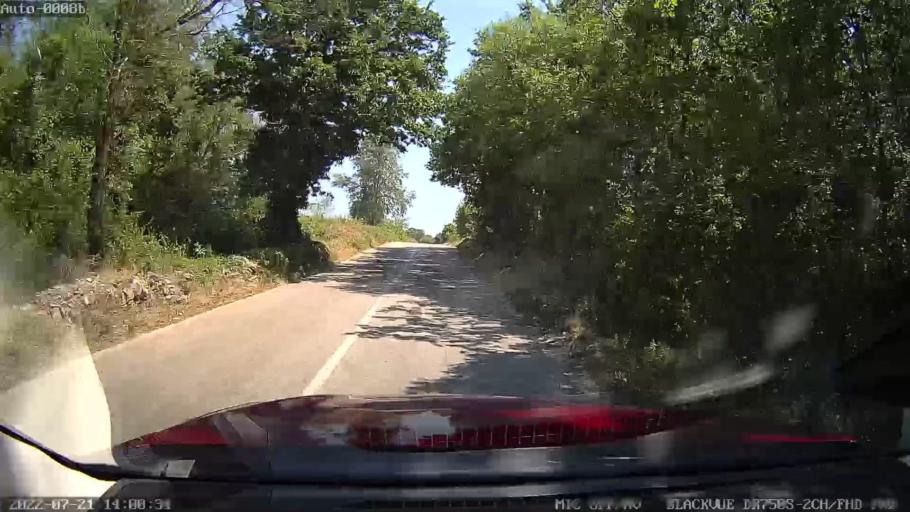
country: HR
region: Istarska
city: Vodnjan
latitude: 45.0977
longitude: 13.8706
